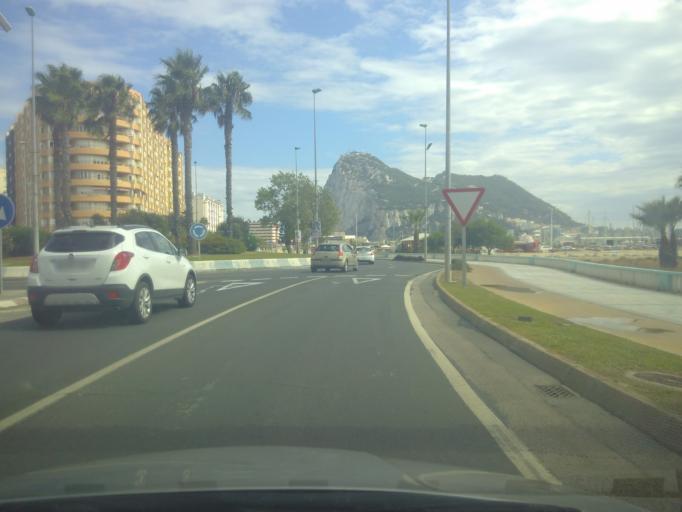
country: ES
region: Andalusia
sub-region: Provincia de Cadiz
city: La Linea de la Concepcion
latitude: 36.1628
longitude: -5.3576
